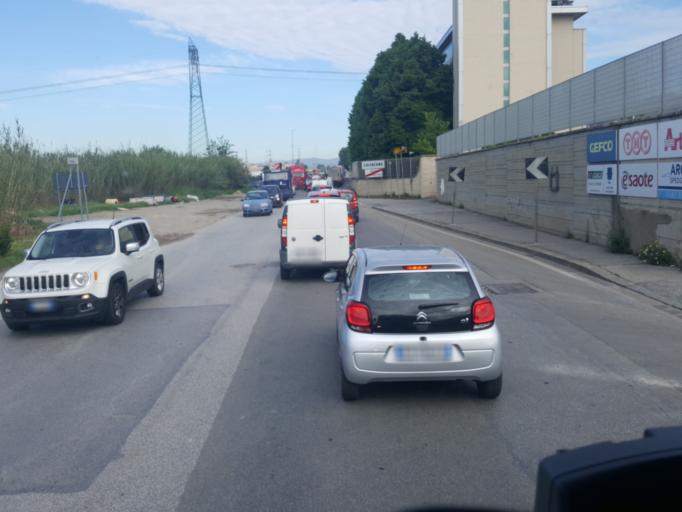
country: IT
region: Tuscany
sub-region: Province of Florence
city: Calenzano
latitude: 43.8433
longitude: 11.1610
